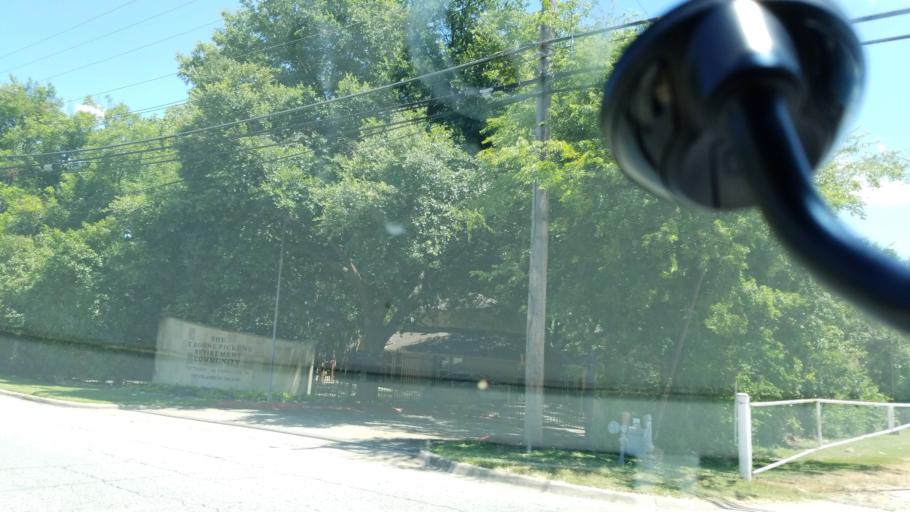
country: US
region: Texas
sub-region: Dallas County
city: Cockrell Hill
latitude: 32.6913
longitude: -96.8185
